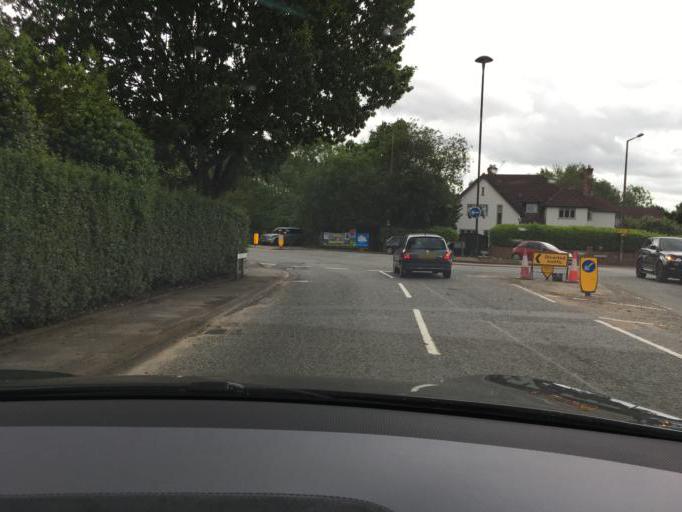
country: GB
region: England
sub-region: Borough of Stockport
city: Bramhall
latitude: 53.3450
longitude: -2.1579
